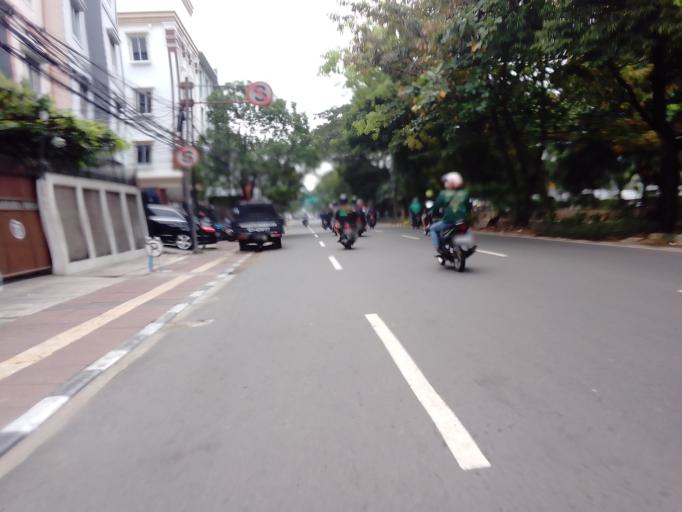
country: ID
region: Jakarta Raya
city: Jakarta
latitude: -6.1653
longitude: 106.8104
